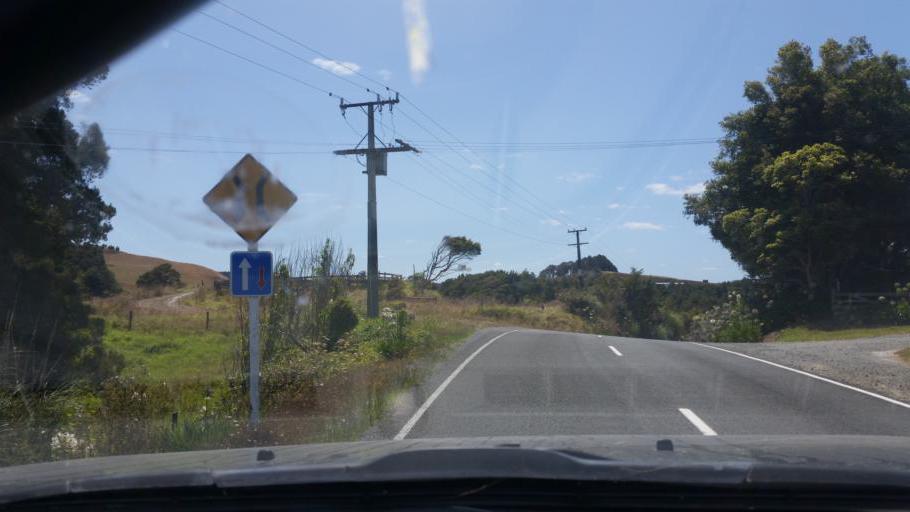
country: NZ
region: Auckland
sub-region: Auckland
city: Wellsford
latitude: -36.1306
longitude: 174.3260
